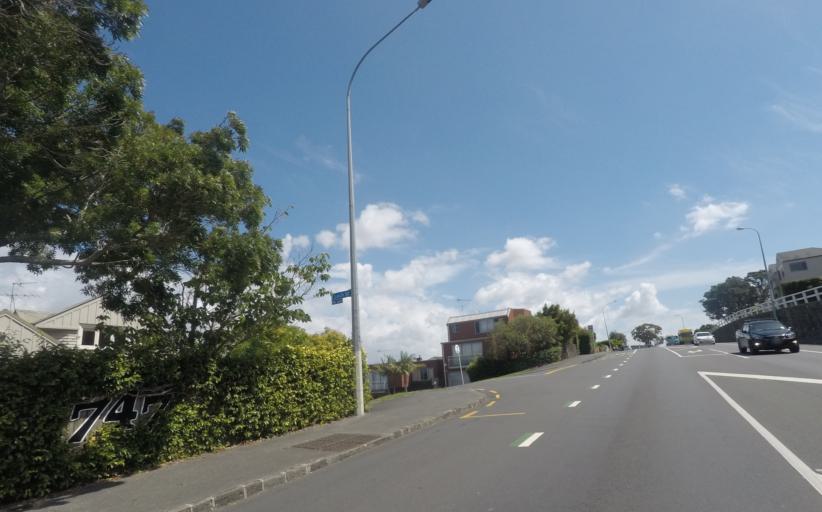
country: NZ
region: Auckland
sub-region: Auckland
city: Tamaki
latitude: -36.8778
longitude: 174.8241
